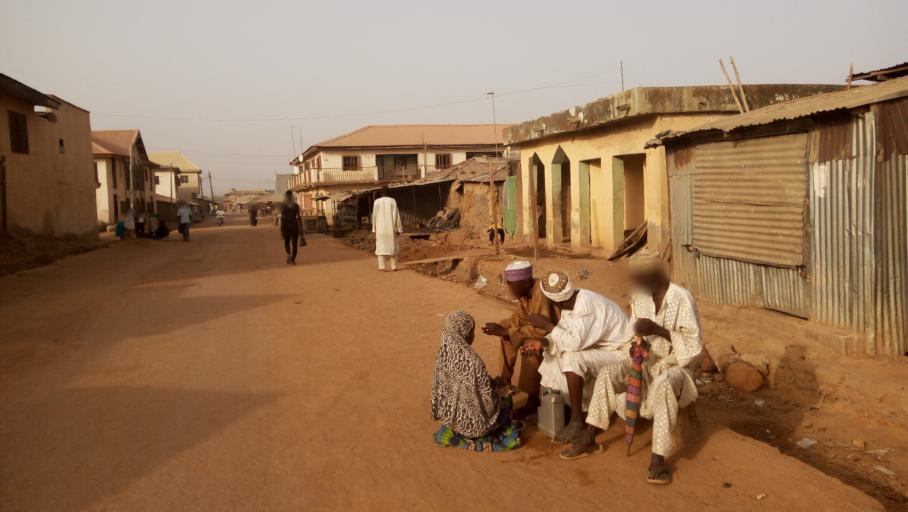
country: NG
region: Kaduna
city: Zaria
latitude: 11.1638
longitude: 7.6505
